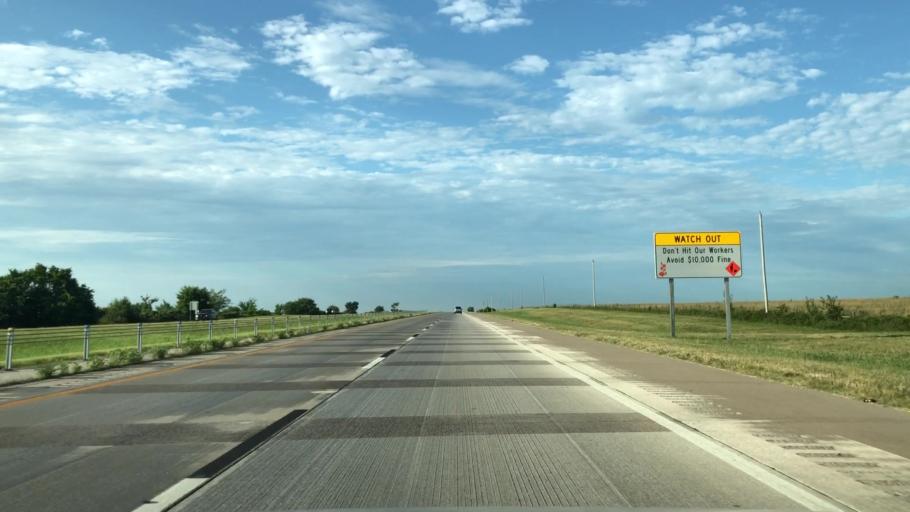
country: US
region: Oklahoma
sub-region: Osage County
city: Skiatook
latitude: 36.4223
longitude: -95.9207
